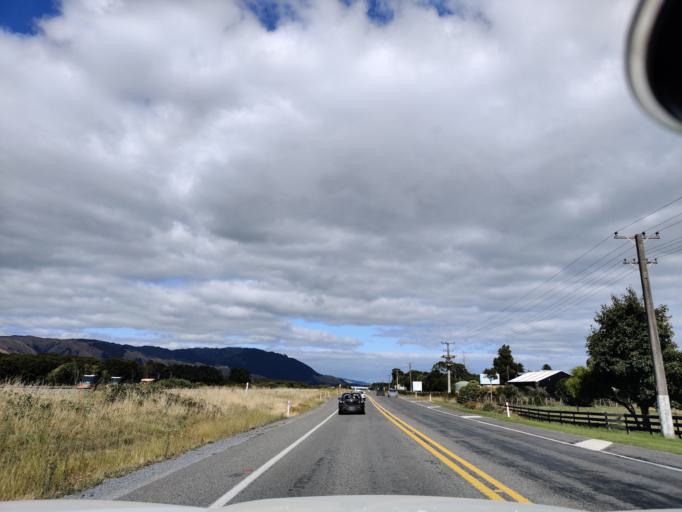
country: NZ
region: Wellington
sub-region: Kapiti Coast District
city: Otaki
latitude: -40.7872
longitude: 175.1332
